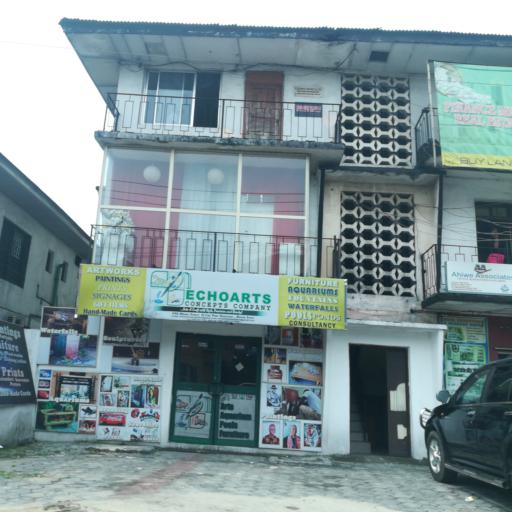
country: NG
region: Rivers
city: Port Harcourt
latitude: 4.8012
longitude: 7.0053
